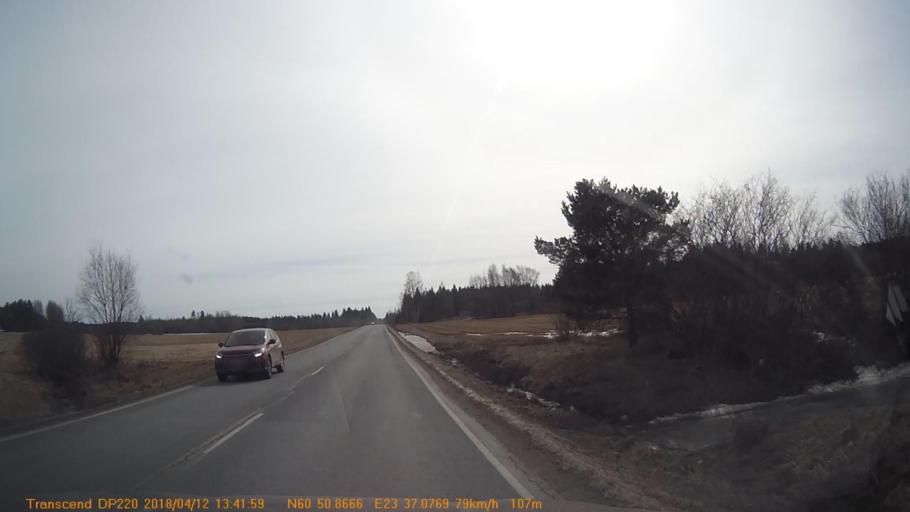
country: FI
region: Haeme
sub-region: Forssa
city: Forssa
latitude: 60.8472
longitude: 23.6180
